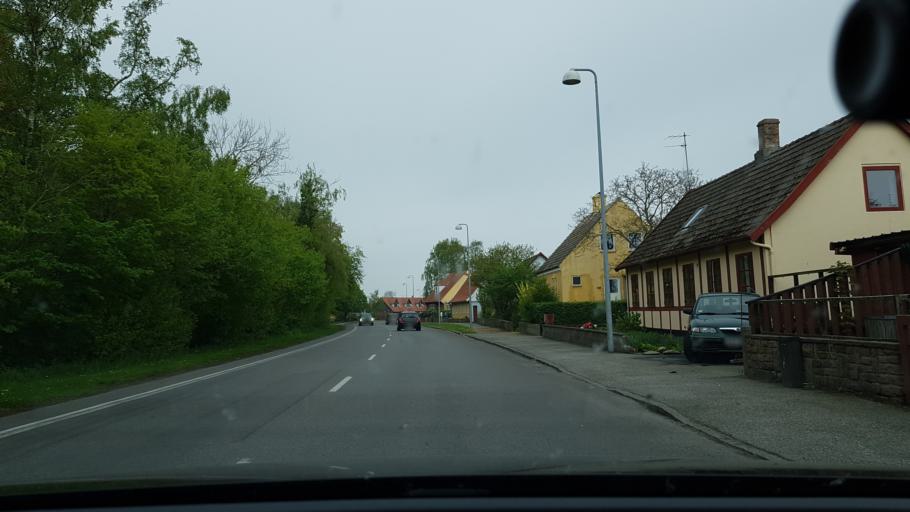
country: DK
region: Capital Region
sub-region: Bornholm Kommune
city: Nexo
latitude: 55.0557
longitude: 15.1261
